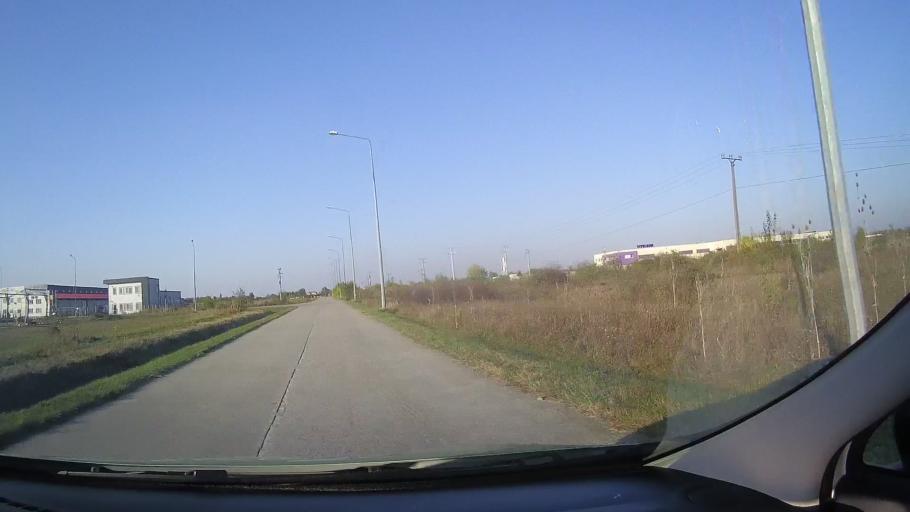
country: RO
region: Bihor
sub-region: Comuna Bors
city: Santion
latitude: 47.1070
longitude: 21.8312
